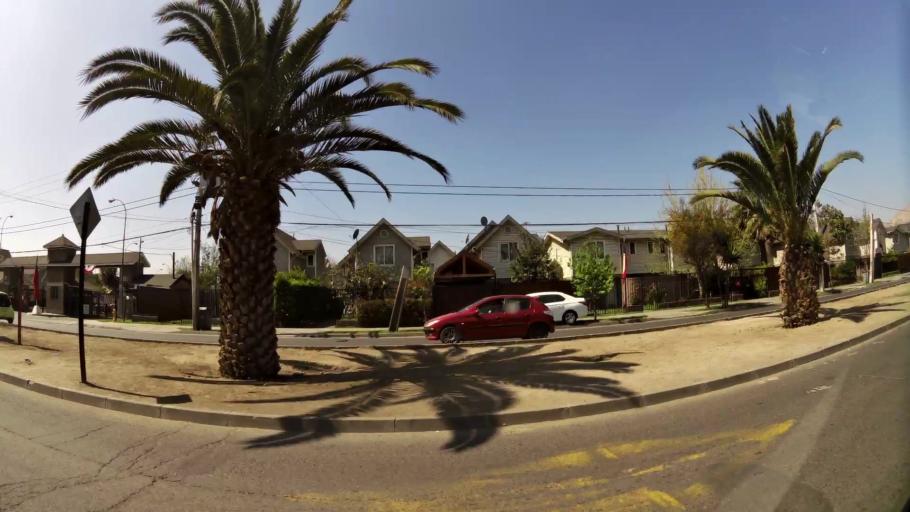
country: CL
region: Santiago Metropolitan
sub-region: Provincia de Santiago
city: Lo Prado
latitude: -33.3640
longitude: -70.7211
